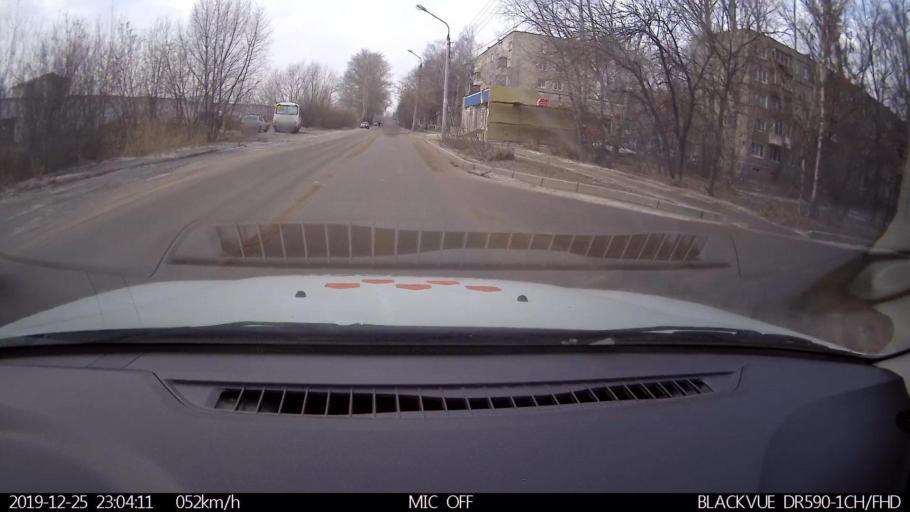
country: RU
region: Nizjnij Novgorod
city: Gorbatovka
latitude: 56.3570
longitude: 43.8133
